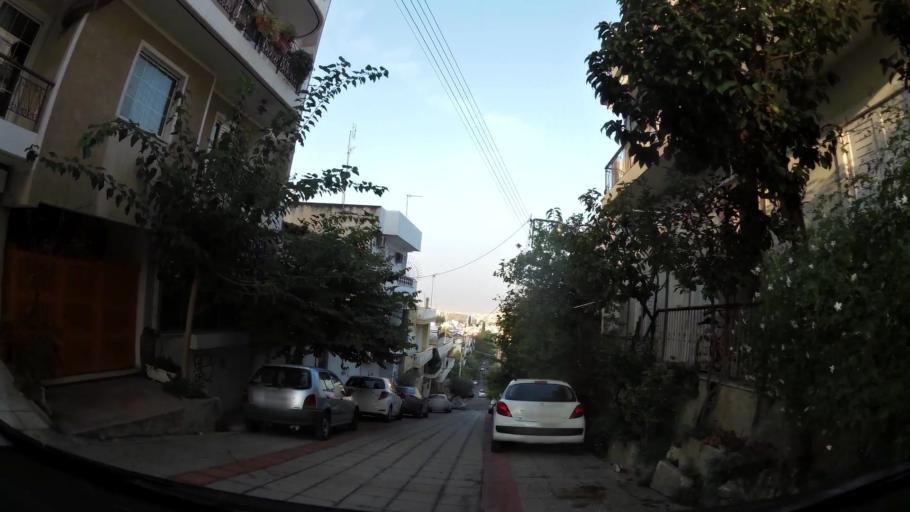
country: GR
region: Attica
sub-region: Nomarchia Athinas
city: Ymittos
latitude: 37.9515
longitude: 23.7547
